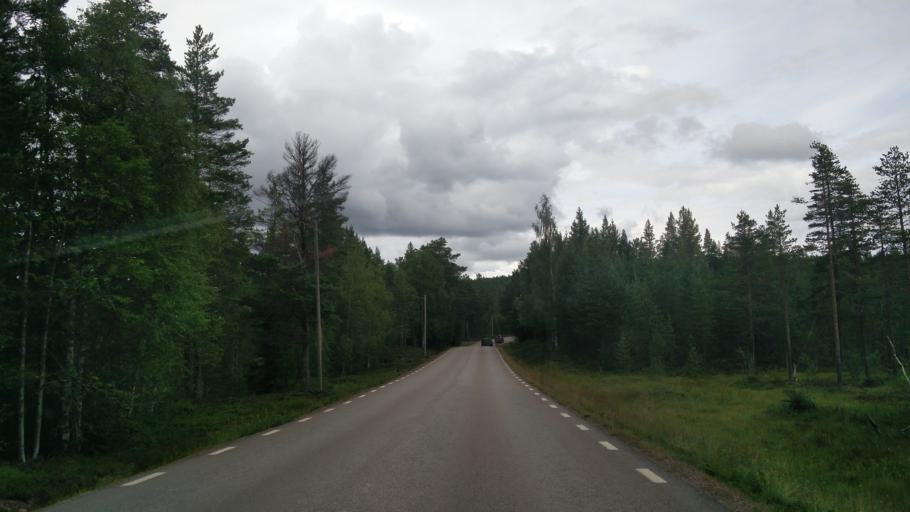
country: NO
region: Hedmark
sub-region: Trysil
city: Innbygda
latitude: 61.1738
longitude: 12.8475
